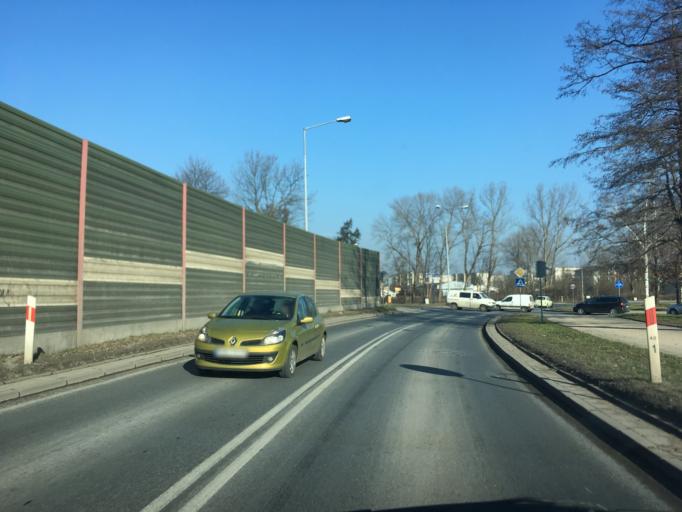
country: PL
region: Lower Silesian Voivodeship
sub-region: Powiat boleslawiecki
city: Boleslawiec
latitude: 51.2683
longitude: 15.5555
